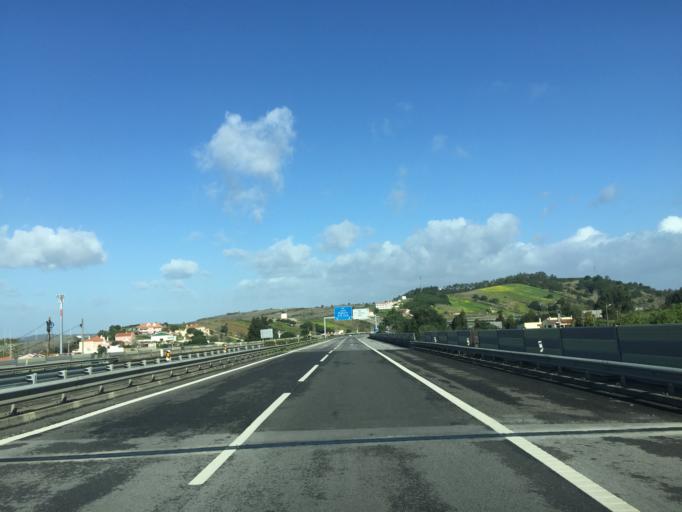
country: PT
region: Lisbon
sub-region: Torres Vedras
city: Torres Vedras
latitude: 39.0590
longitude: -9.2393
